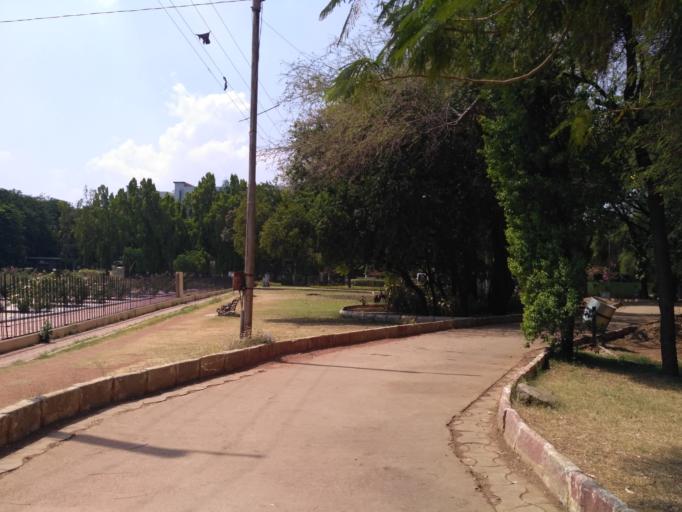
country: IN
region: Telangana
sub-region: Hyderabad
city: Hyderabad
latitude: 17.4124
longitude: 78.4816
